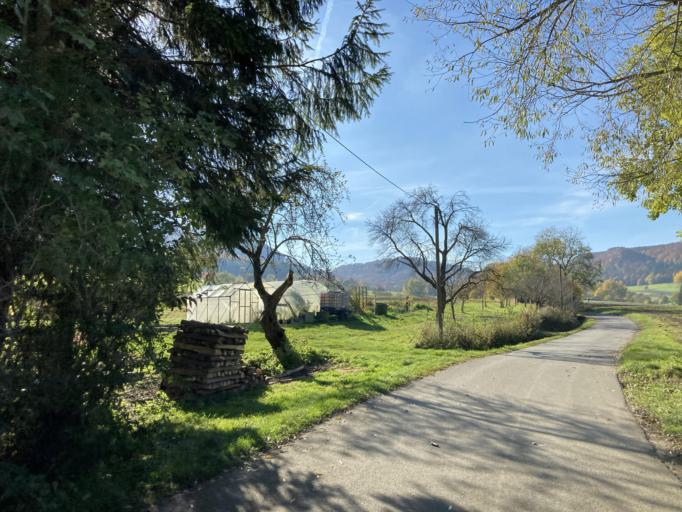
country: DE
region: Baden-Wuerttemberg
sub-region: Tuebingen Region
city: Mossingen
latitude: 48.3785
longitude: 9.0986
